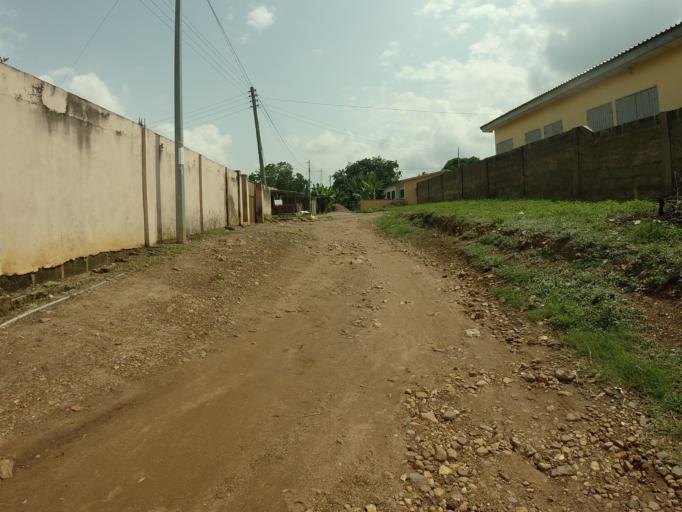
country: GH
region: Volta
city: Ho
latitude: 6.6138
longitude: 0.4764
